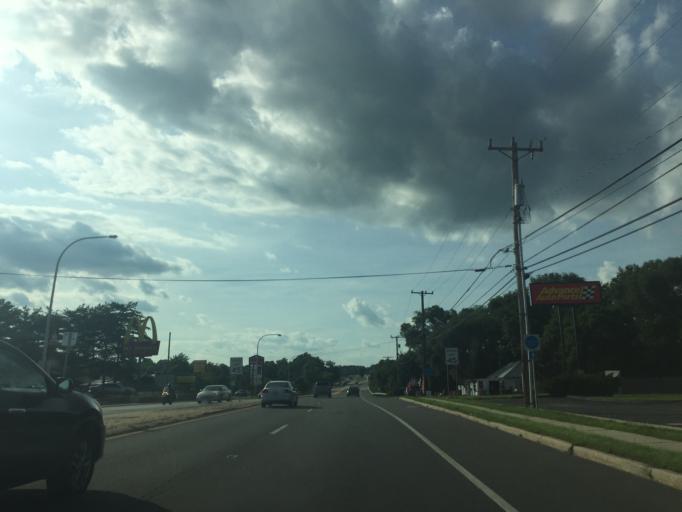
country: US
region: Delaware
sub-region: Kent County
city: Smyrna
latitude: 39.3066
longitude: -75.6072
